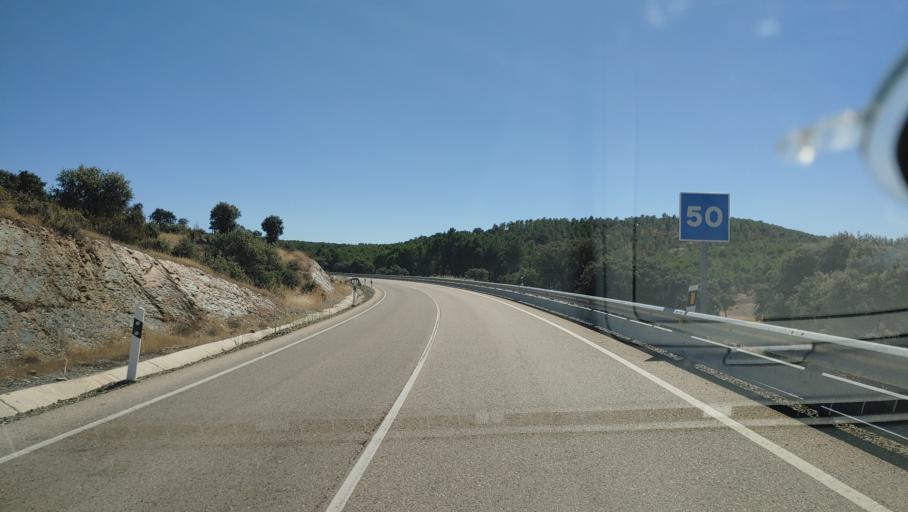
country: ES
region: Andalusia
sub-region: Provincia de Jaen
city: Genave
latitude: 38.4909
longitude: -2.7674
